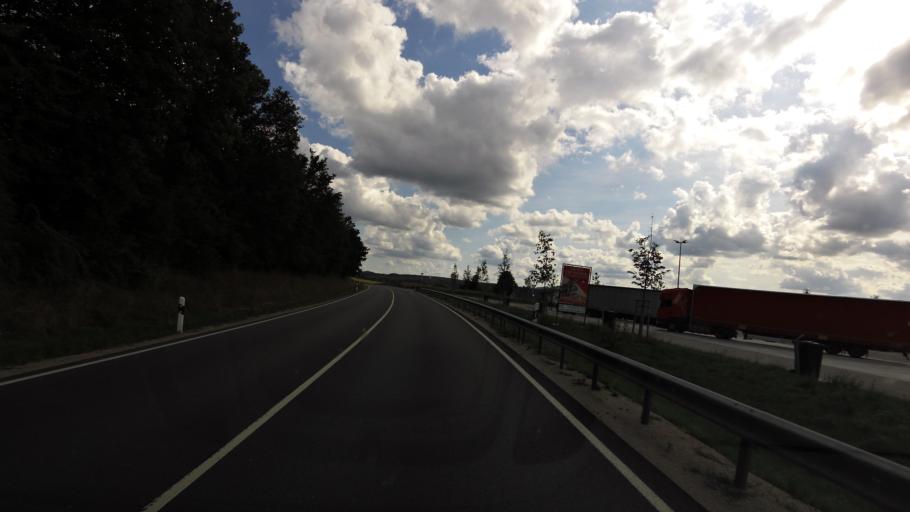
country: DE
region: Bavaria
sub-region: Upper Palatinate
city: Cham
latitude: 49.1958
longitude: 12.6558
